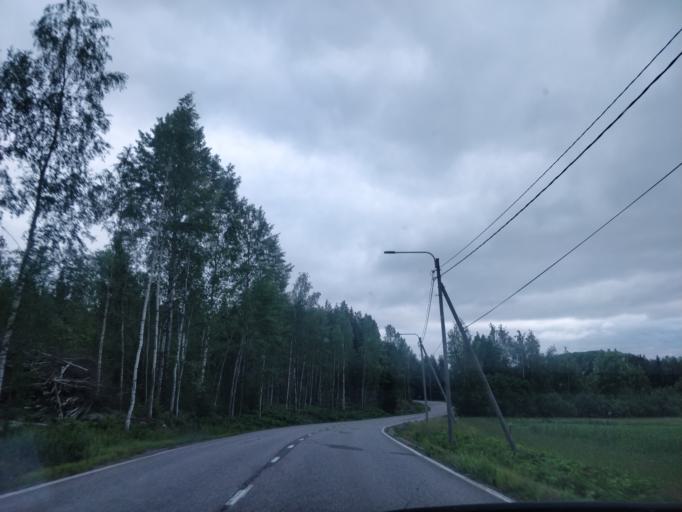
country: FI
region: Uusimaa
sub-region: Helsinki
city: Kauniainen
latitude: 60.2799
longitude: 24.7122
